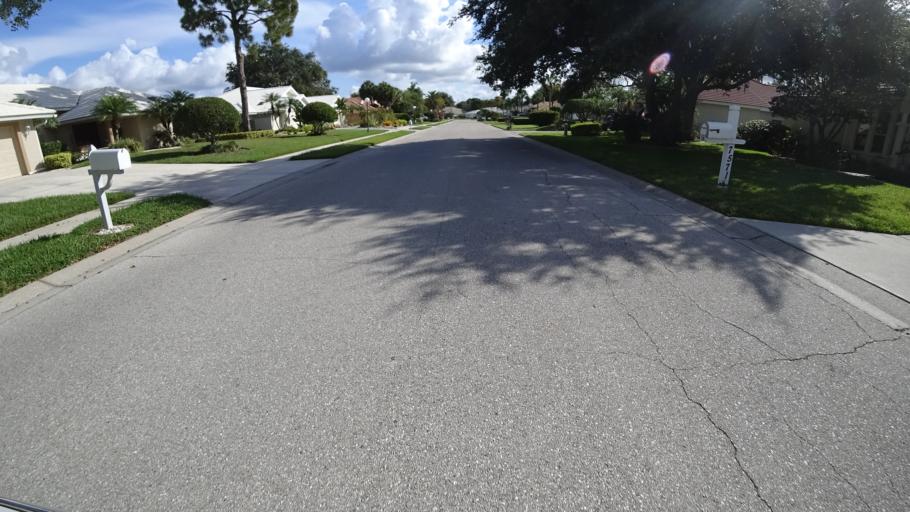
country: US
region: Florida
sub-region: Sarasota County
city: Desoto Lakes
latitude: 27.4054
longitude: -82.4827
